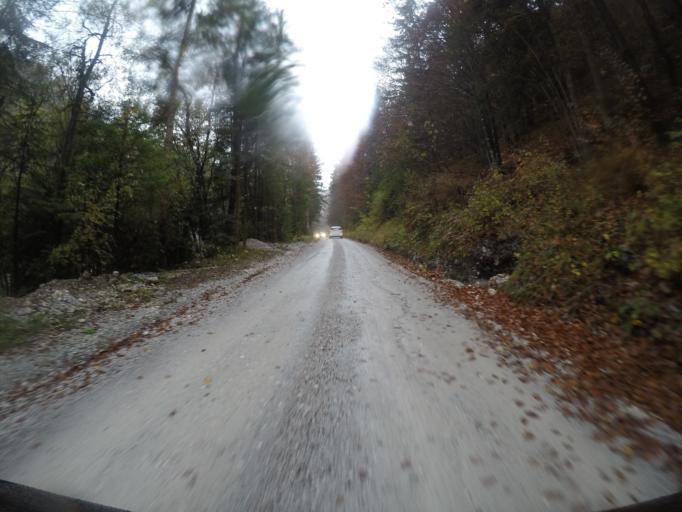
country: SI
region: Kranjska Gora
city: Mojstrana
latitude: 46.4378
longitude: 13.8939
